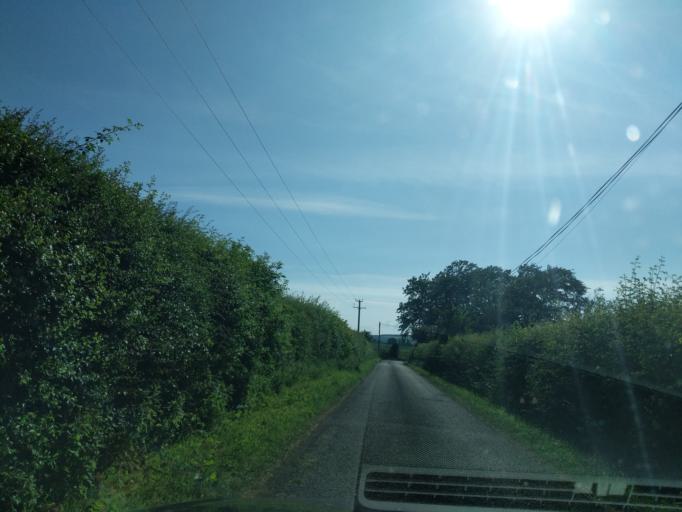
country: GB
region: Scotland
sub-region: Fife
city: Pathhead
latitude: 55.8778
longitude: -2.9493
